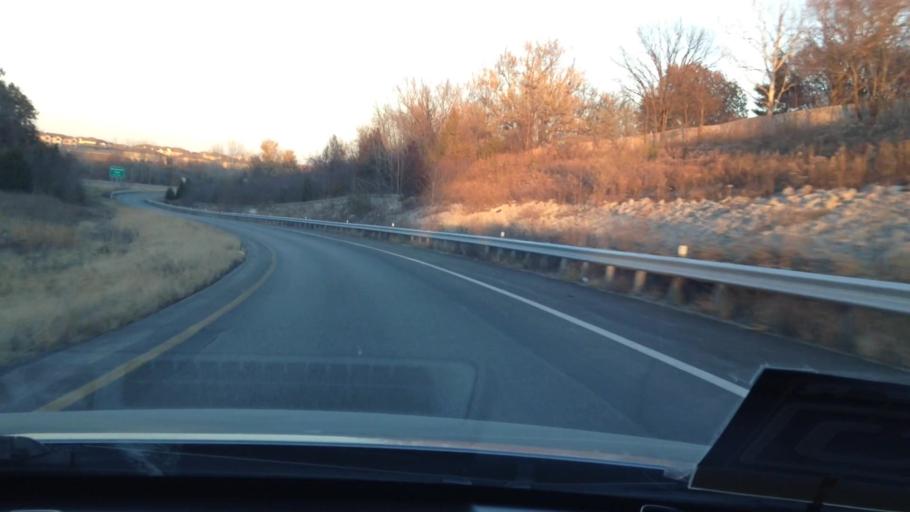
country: US
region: Missouri
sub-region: Clay County
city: Gladstone
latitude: 39.2579
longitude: -94.5856
